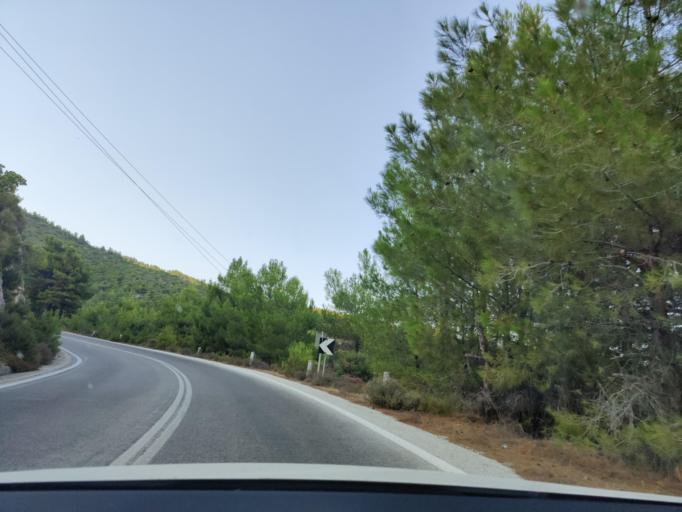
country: GR
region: East Macedonia and Thrace
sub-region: Nomos Kavalas
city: Potamia
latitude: 40.6226
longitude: 24.7621
